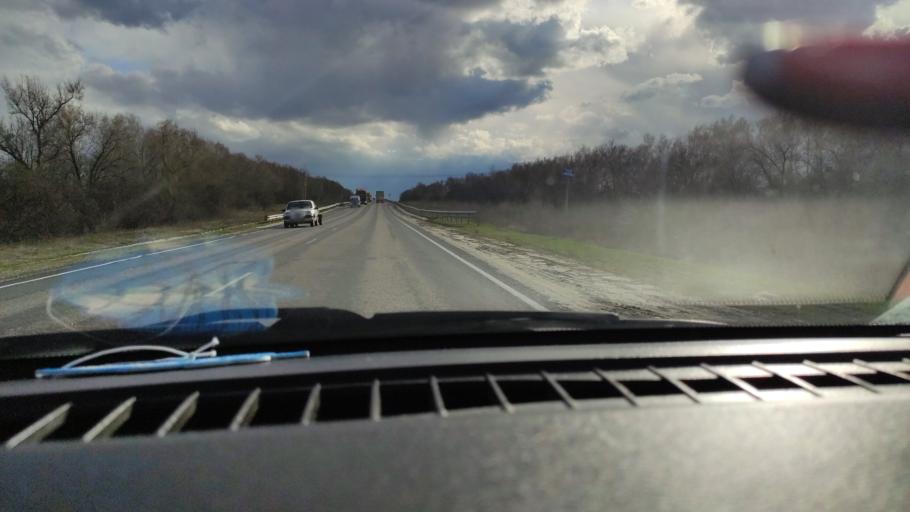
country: RU
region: Saratov
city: Sinodskoye
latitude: 51.9620
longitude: 46.6259
